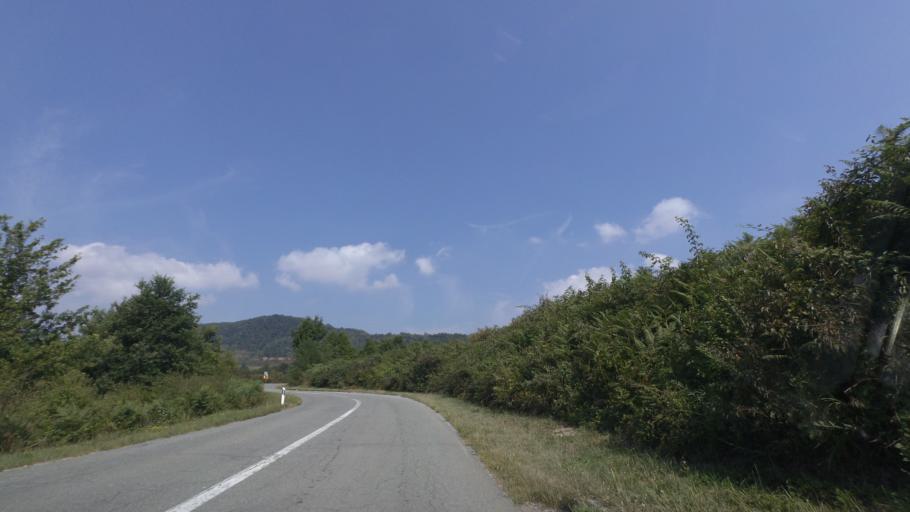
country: BA
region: Federation of Bosnia and Herzegovina
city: Zboriste
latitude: 45.1437
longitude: 16.1581
